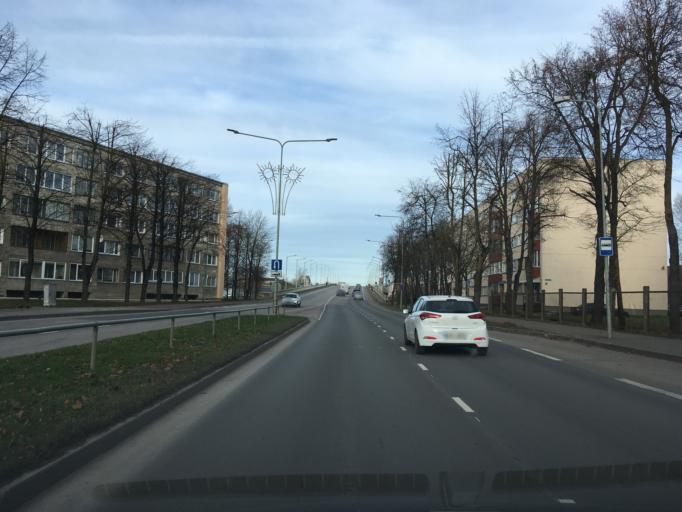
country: EE
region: Ida-Virumaa
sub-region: Narva linn
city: Narva
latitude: 59.3690
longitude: 28.1856
